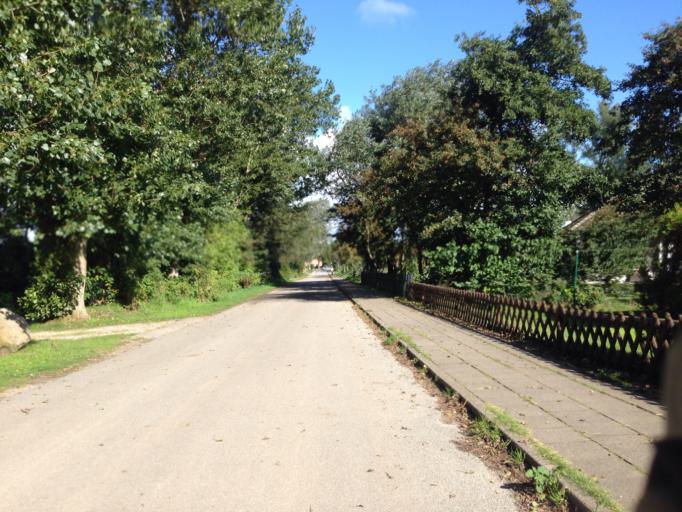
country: DE
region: Schleswig-Holstein
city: Borgsum
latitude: 54.6861
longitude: 8.4684
